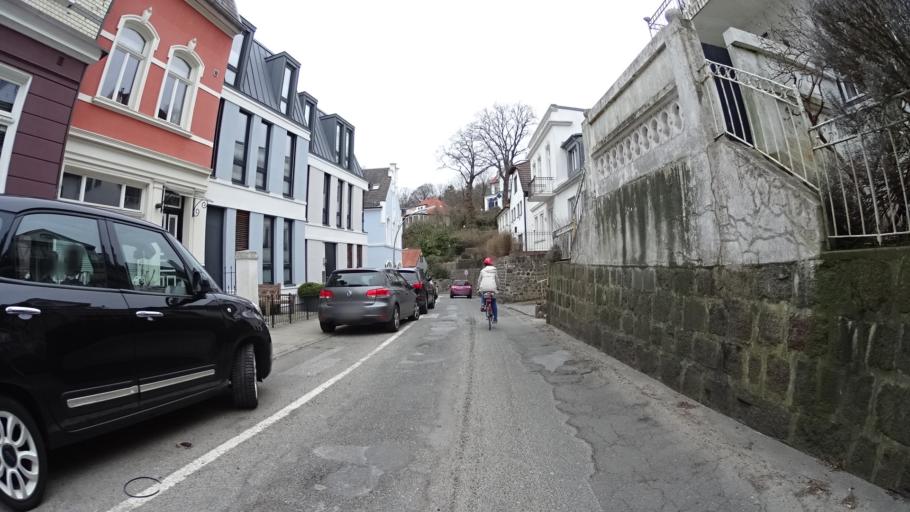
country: DE
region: Schleswig-Holstein
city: Halstenbek
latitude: 53.5595
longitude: 9.8050
